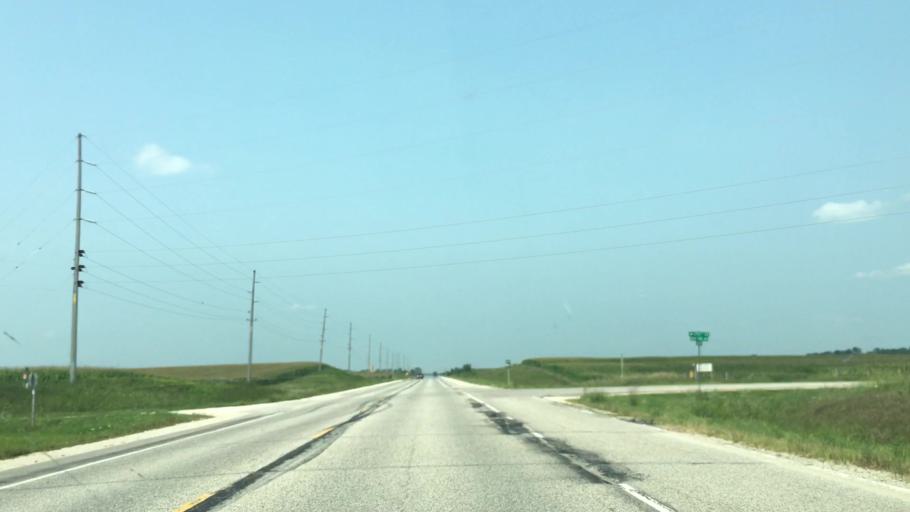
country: US
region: Iowa
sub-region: Fayette County
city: Fayette
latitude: 42.8833
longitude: -91.8105
